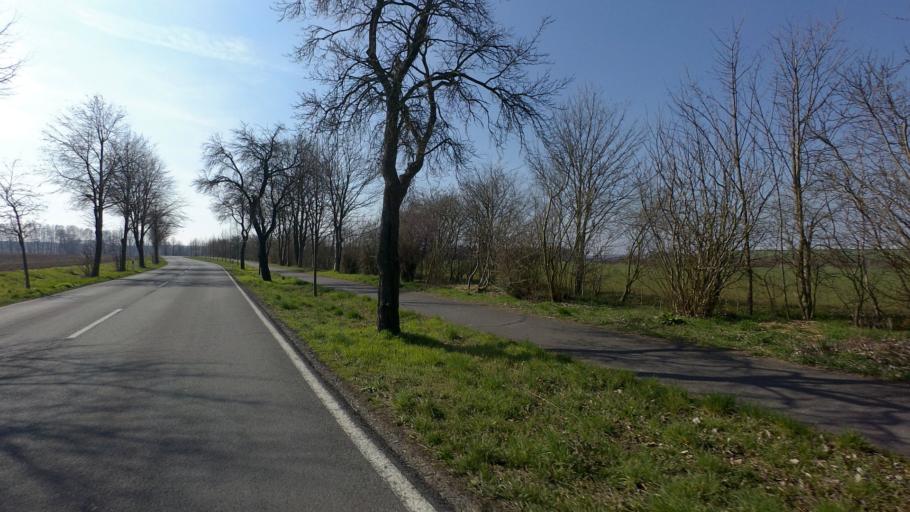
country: DE
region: Brandenburg
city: Golssen
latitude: 51.9673
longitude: 13.5985
